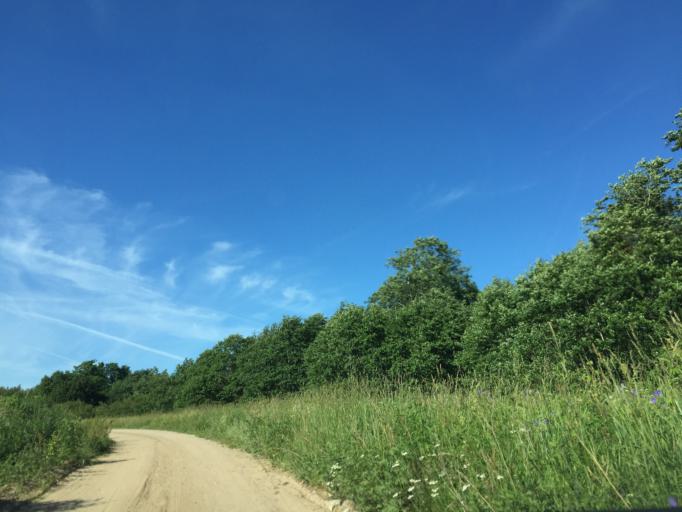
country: LV
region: Kuldigas Rajons
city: Kuldiga
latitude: 57.0732
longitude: 21.8263
